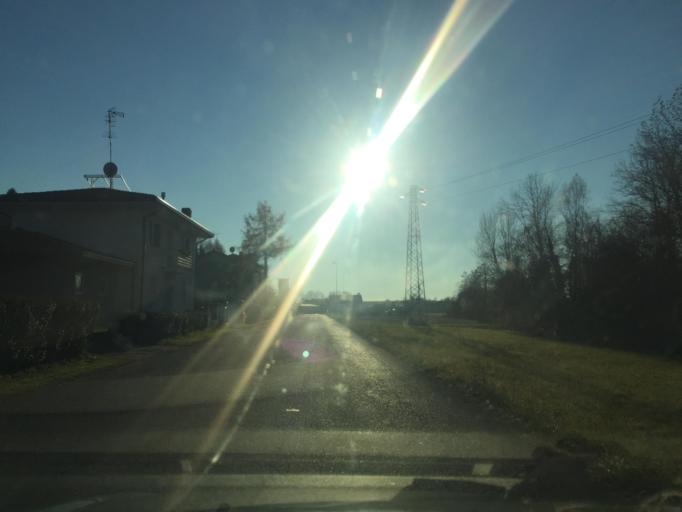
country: IT
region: Friuli Venezia Giulia
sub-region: Provincia di Udine
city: Buia
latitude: 46.2196
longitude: 13.1060
